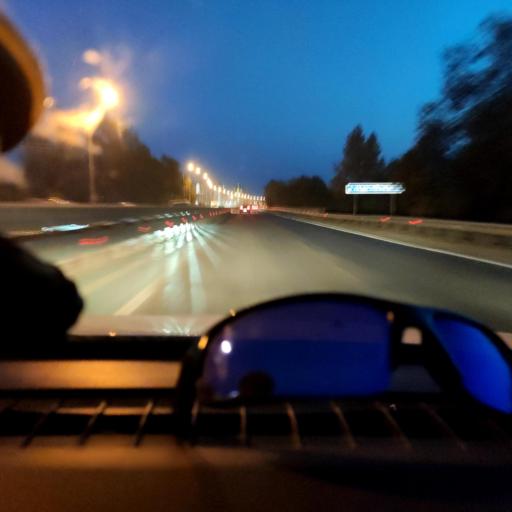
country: RU
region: Samara
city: Samara
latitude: 53.1053
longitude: 50.1630
